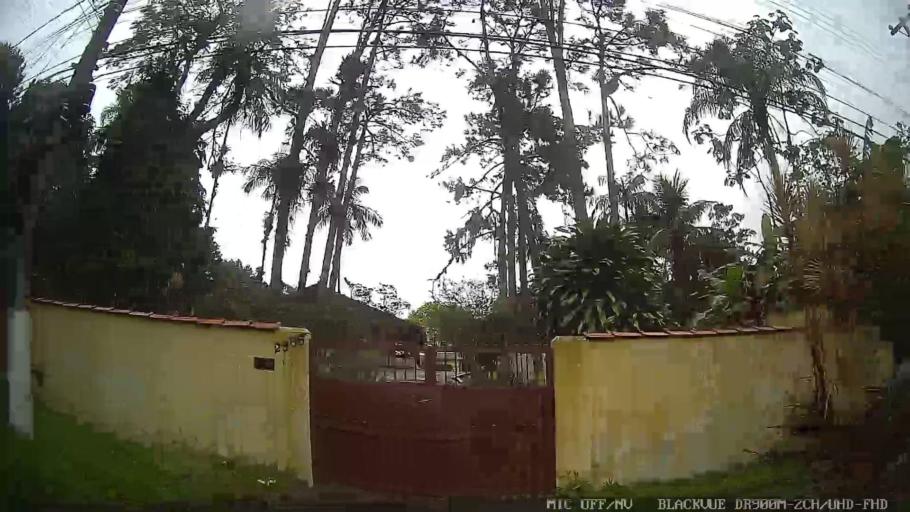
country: BR
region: Sao Paulo
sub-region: Itanhaem
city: Itanhaem
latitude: -24.1760
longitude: -46.8303
